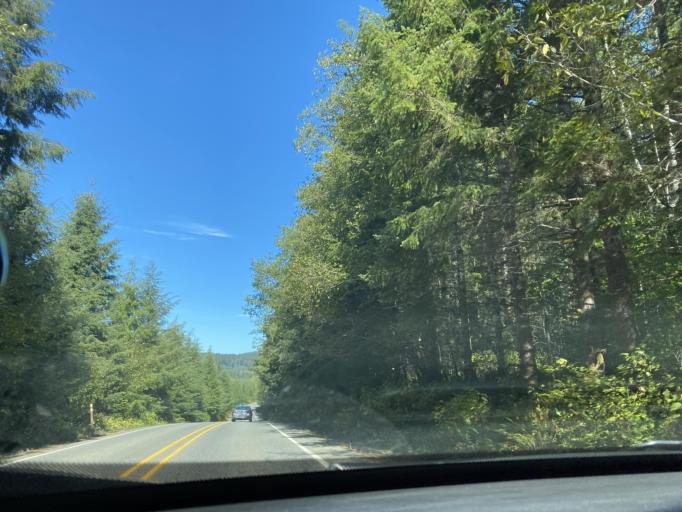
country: US
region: Washington
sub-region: Clallam County
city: Forks
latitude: 47.9470
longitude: -124.4624
